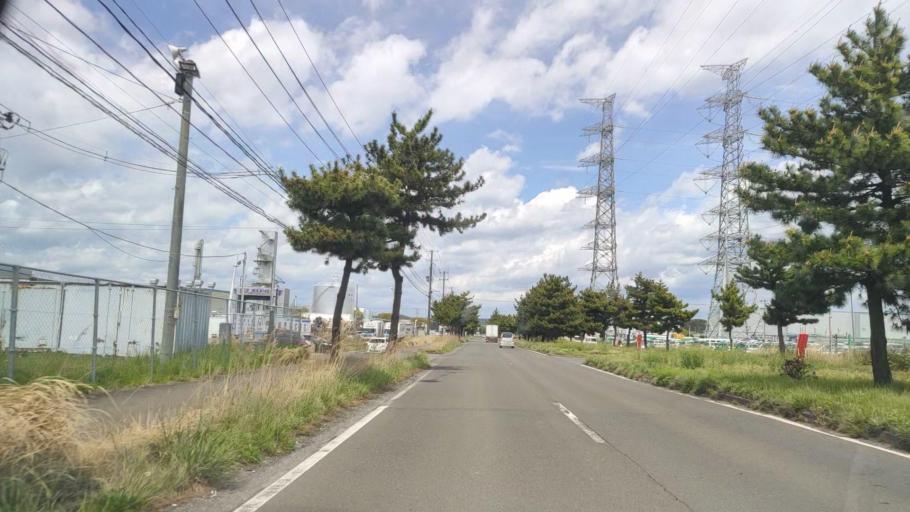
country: JP
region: Miyagi
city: Shiogama
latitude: 38.2845
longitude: 141.0246
